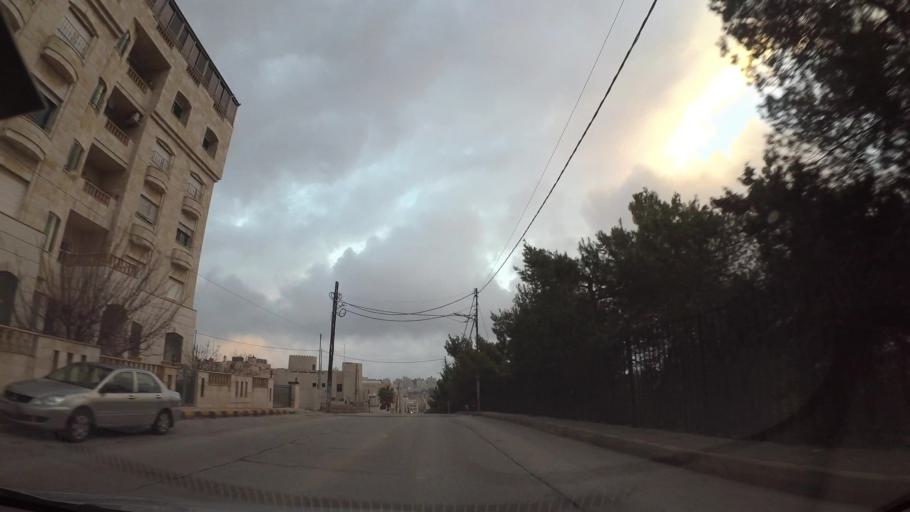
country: JO
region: Amman
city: Al Jubayhah
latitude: 32.0097
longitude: 35.8787
